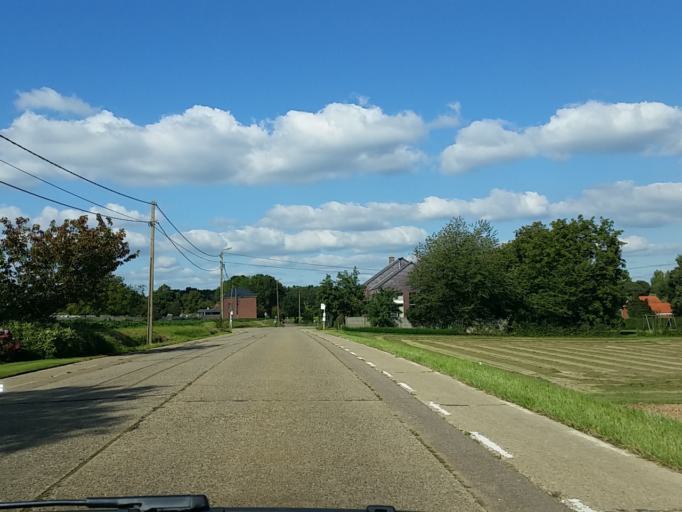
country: BE
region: Flanders
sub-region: Provincie Vlaams-Brabant
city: Lubbeek
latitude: 50.9147
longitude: 4.8416
